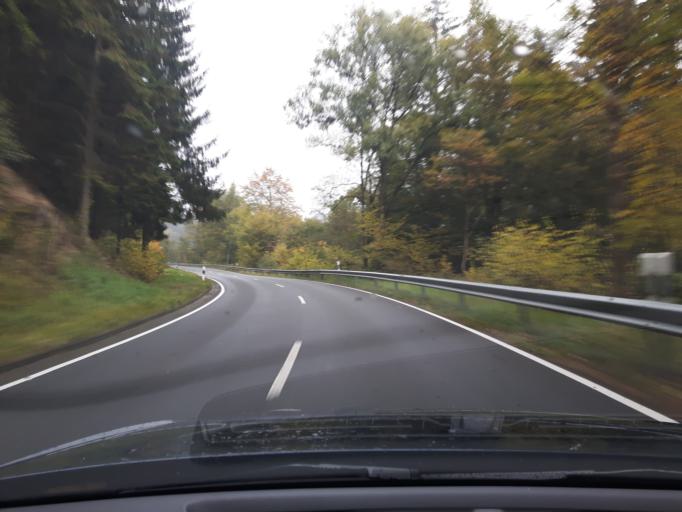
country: DE
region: North Rhine-Westphalia
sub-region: Regierungsbezirk Arnsberg
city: Bad Laasphe
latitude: 50.9580
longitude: 8.3929
